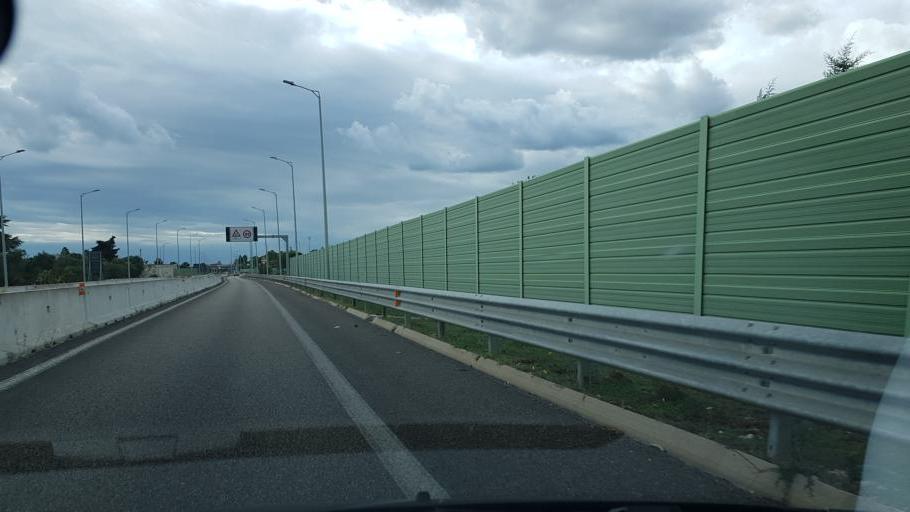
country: IT
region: Apulia
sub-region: Provincia di Lecce
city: Maglie
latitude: 40.1236
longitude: 18.3223
